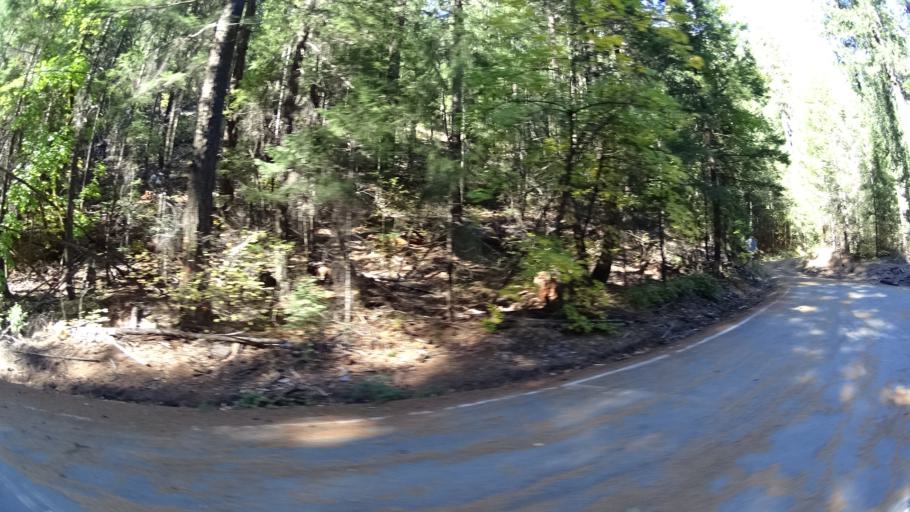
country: US
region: California
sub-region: Trinity County
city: Weaverville
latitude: 41.2030
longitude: -123.0715
